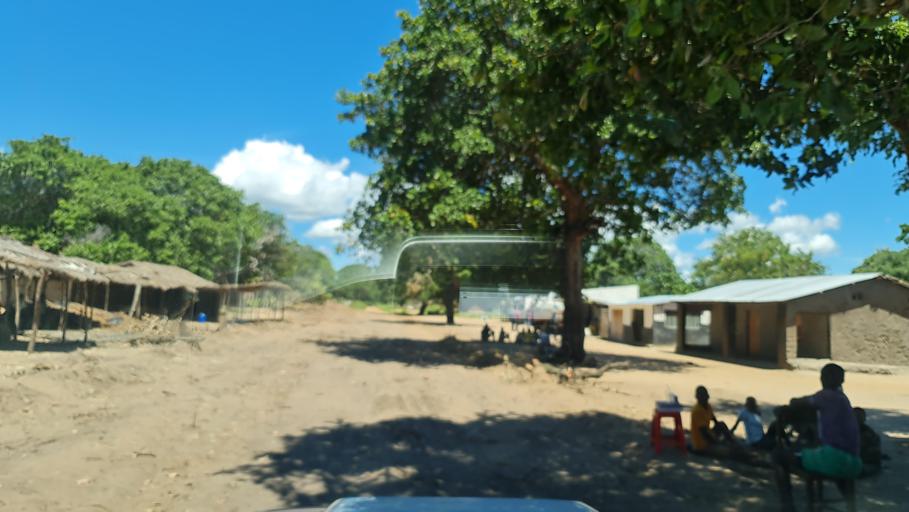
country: MZ
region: Nampula
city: Nampula
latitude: -15.2996
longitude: 39.8644
